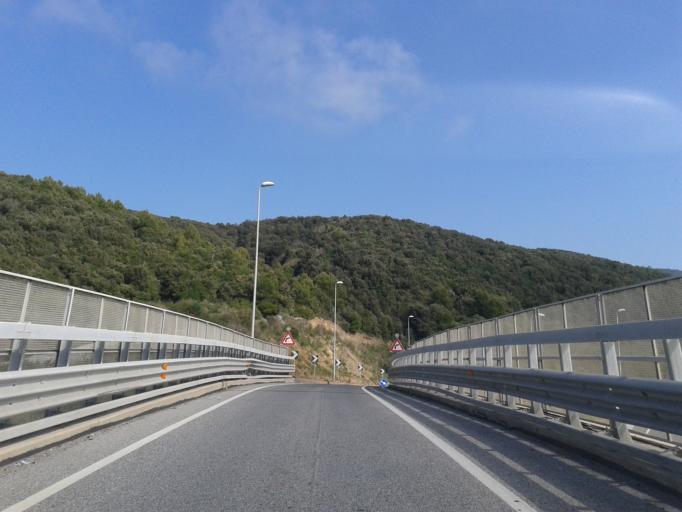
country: IT
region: Tuscany
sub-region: Provincia di Livorno
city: Quercianella
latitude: 43.4836
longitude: 10.3343
